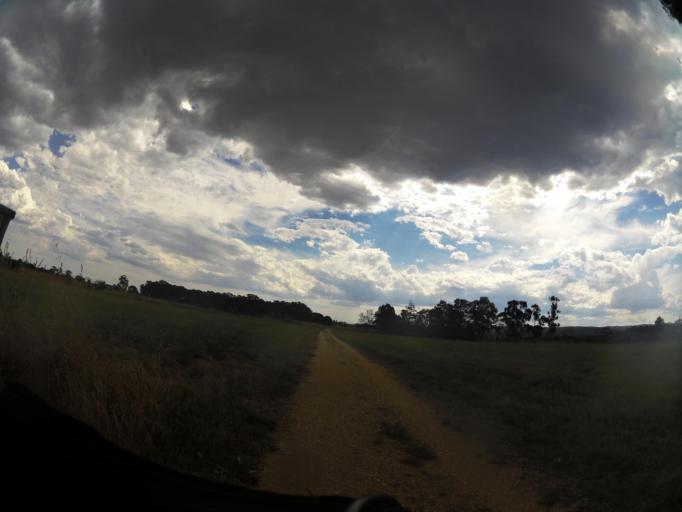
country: AU
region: Victoria
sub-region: Wellington
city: Heyfield
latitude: -38.0153
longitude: 146.6907
